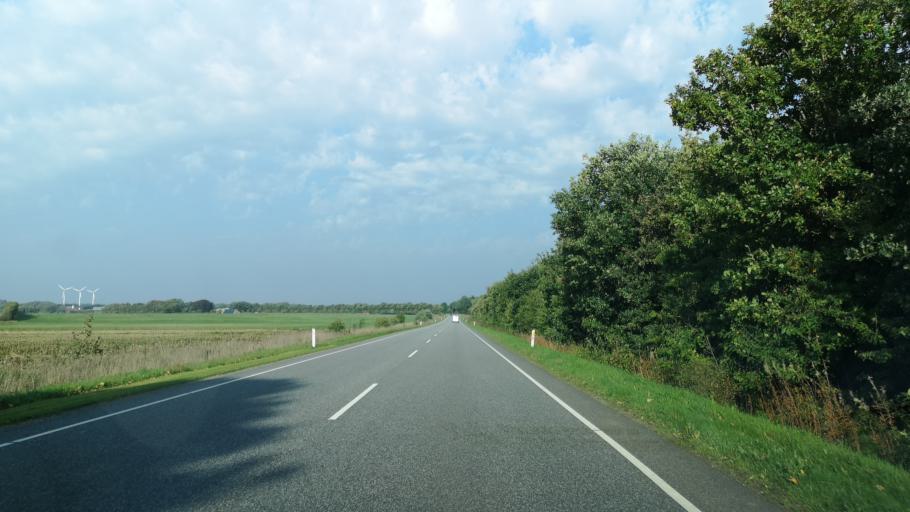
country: DK
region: Central Jutland
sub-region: Herning Kommune
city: Kibaek
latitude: 55.9777
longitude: 8.8278
